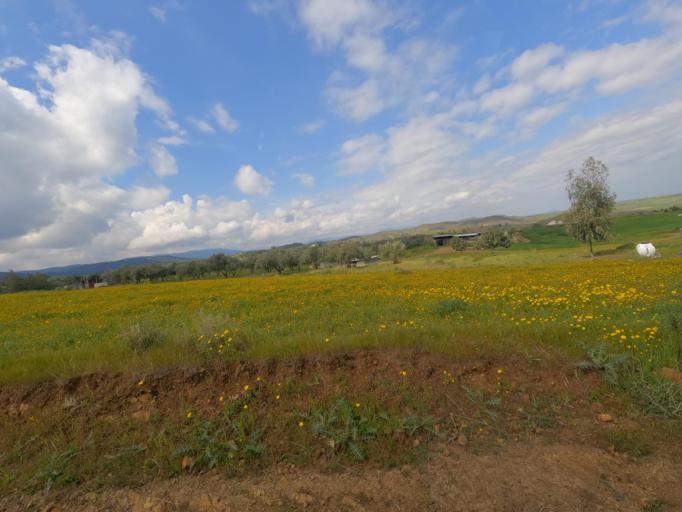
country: CY
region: Lefkosia
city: Astromeritis
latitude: 35.0783
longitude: 32.9610
